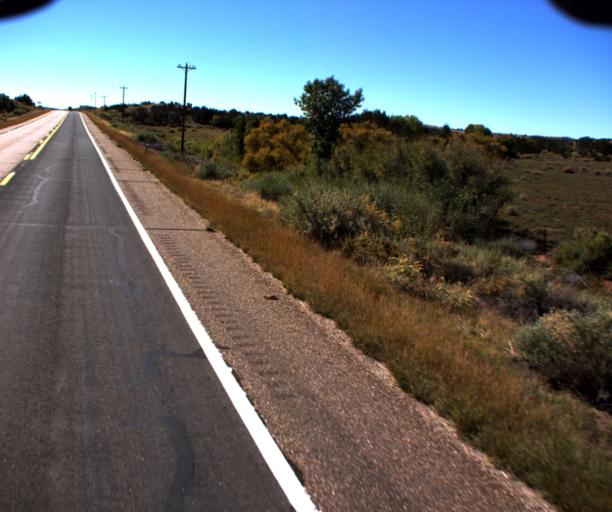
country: US
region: Arizona
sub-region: Apache County
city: Saint Johns
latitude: 34.4071
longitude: -109.4108
